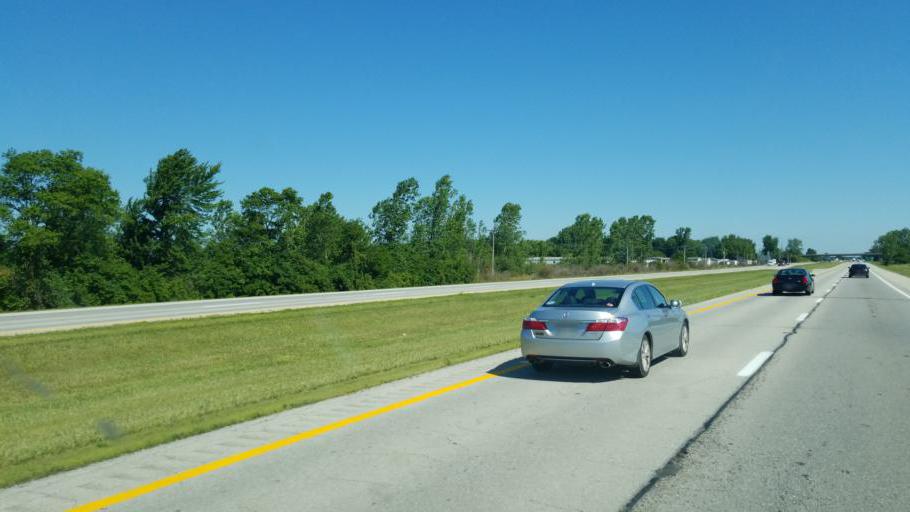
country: US
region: Ohio
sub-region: Marion County
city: Marion
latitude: 40.6234
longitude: -83.0959
